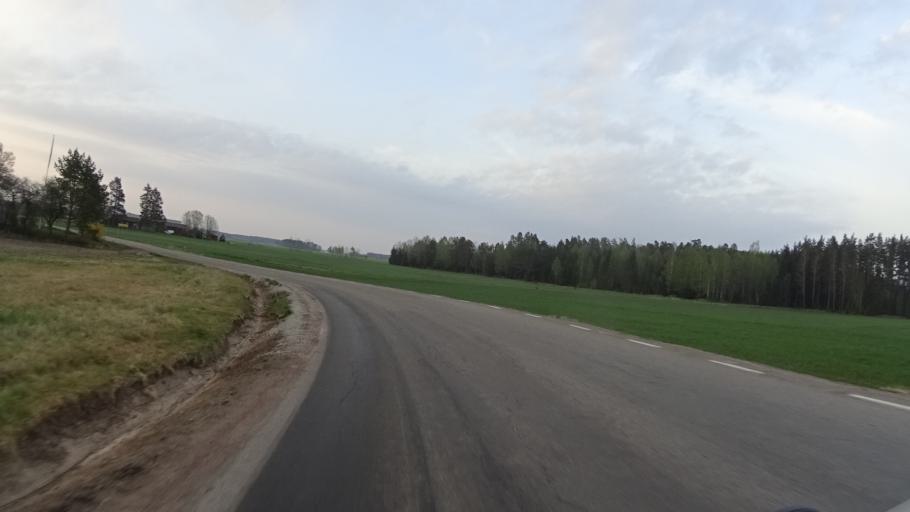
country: SE
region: Vaestra Goetaland
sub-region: Gotene Kommun
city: Kallby
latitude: 58.4815
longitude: 13.3164
